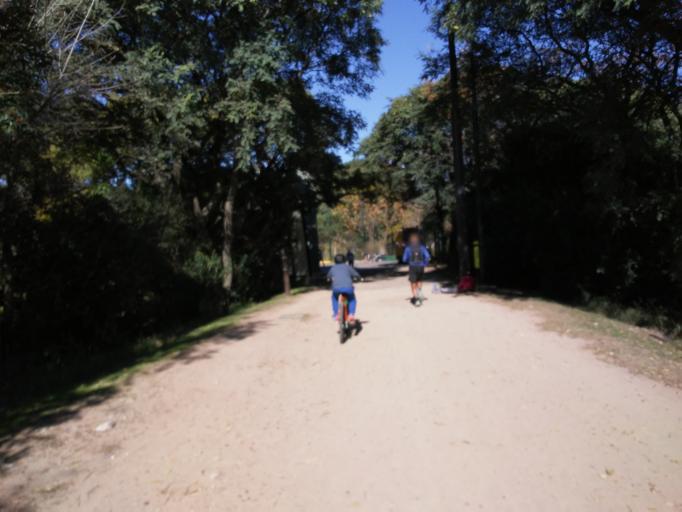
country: AR
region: Buenos Aires F.D.
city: Buenos Aires
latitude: -34.6156
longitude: -58.3552
